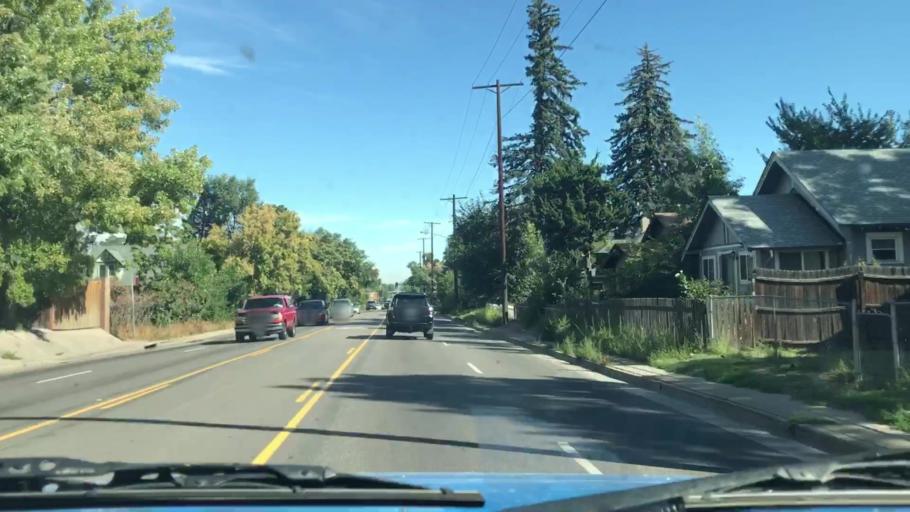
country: US
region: Colorado
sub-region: Jefferson County
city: Edgewater
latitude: 39.7711
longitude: -105.0532
